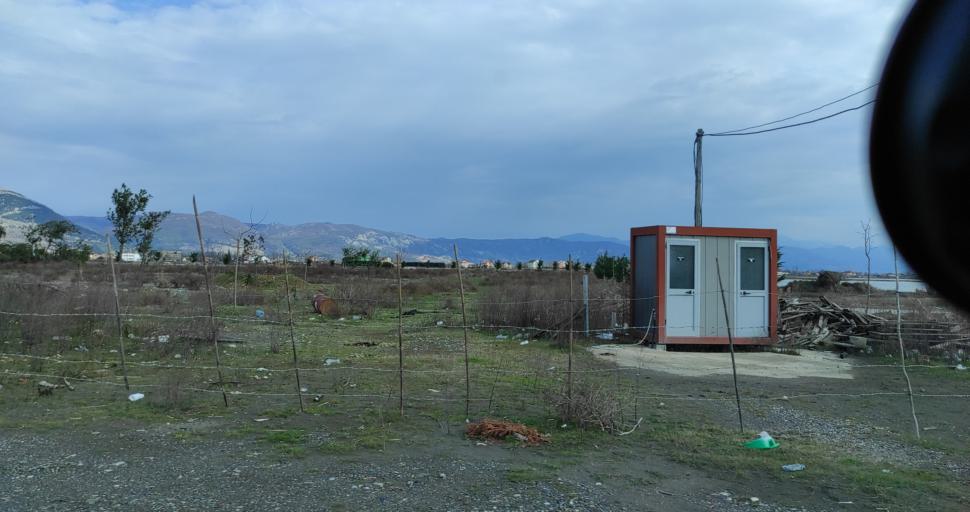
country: AL
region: Lezhe
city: Shengjin
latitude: 41.7710
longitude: 19.6009
